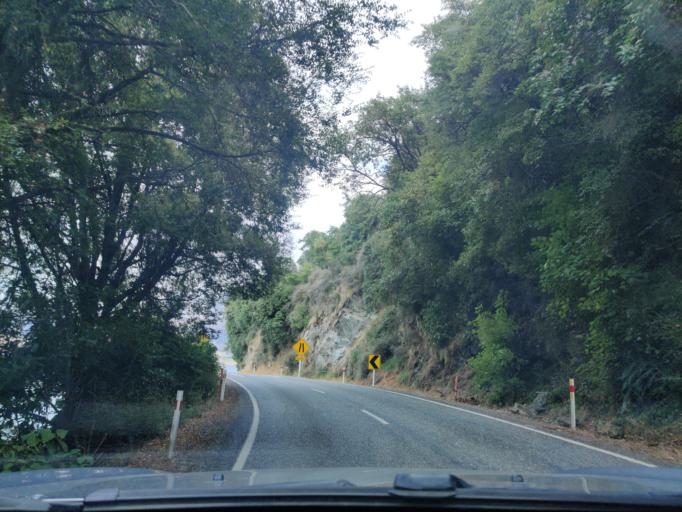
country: NZ
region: Otago
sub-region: Queenstown-Lakes District
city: Queenstown
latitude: -45.0791
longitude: 168.4820
